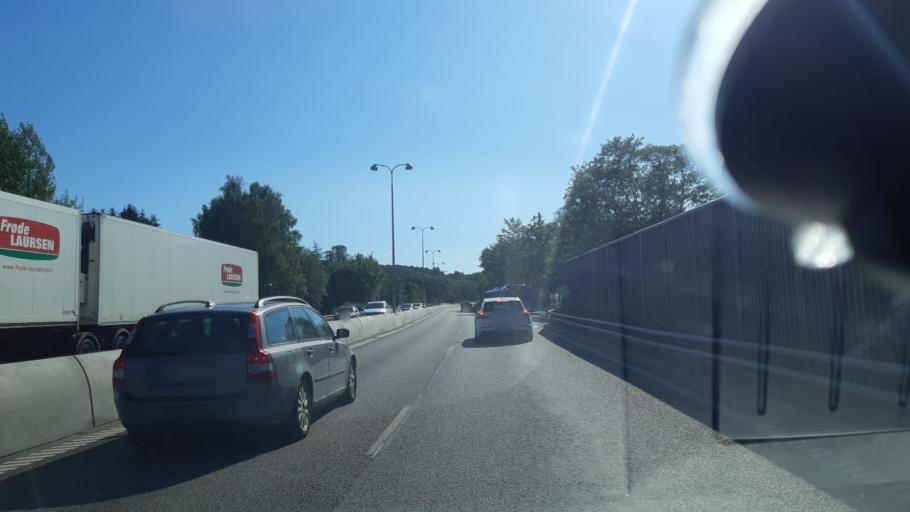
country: SE
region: Vaestra Goetaland
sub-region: Goteborg
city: Eriksbo
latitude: 57.7745
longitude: 12.0563
